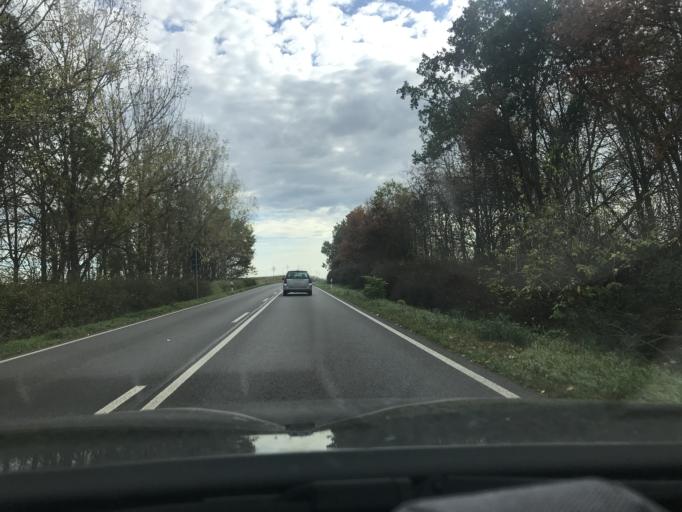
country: DE
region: Thuringia
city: Westhausen
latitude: 51.0236
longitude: 10.6795
